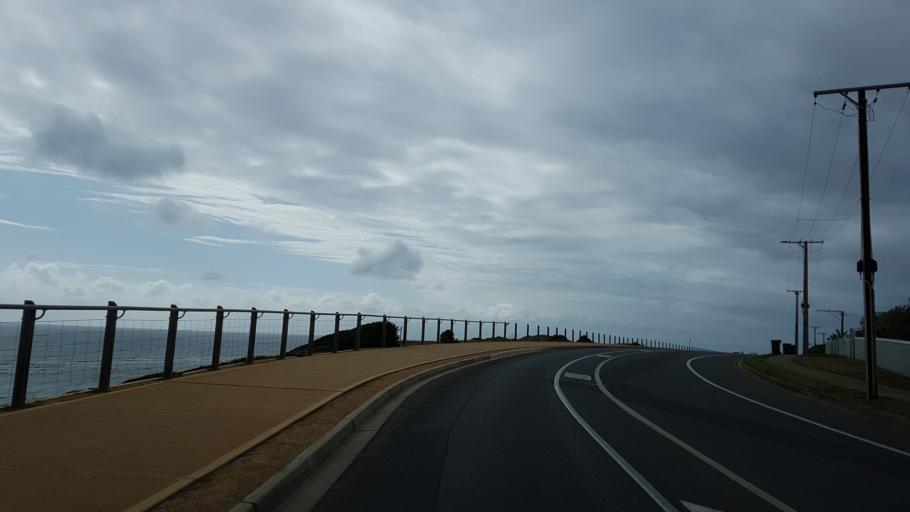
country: AU
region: South Australia
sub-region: Onkaparinga
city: Port Willunga
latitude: -35.2860
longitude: 138.4444
